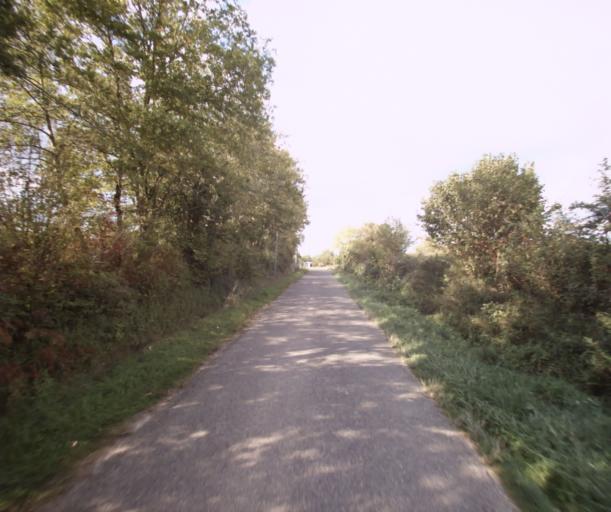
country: FR
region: Midi-Pyrenees
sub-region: Departement du Gers
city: Cazaubon
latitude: 43.8900
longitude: -0.0410
